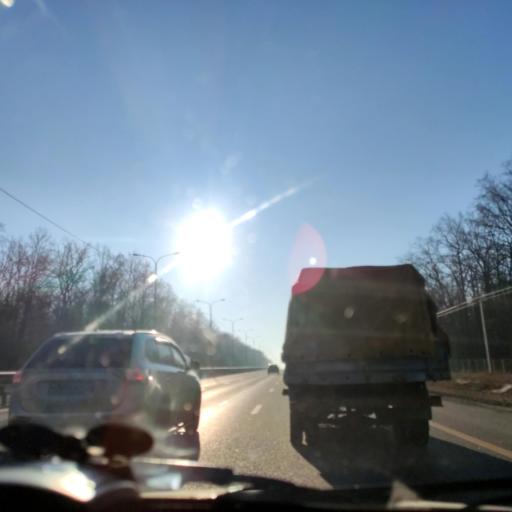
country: RU
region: Voronezj
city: Ramon'
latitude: 51.8652
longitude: 39.2158
